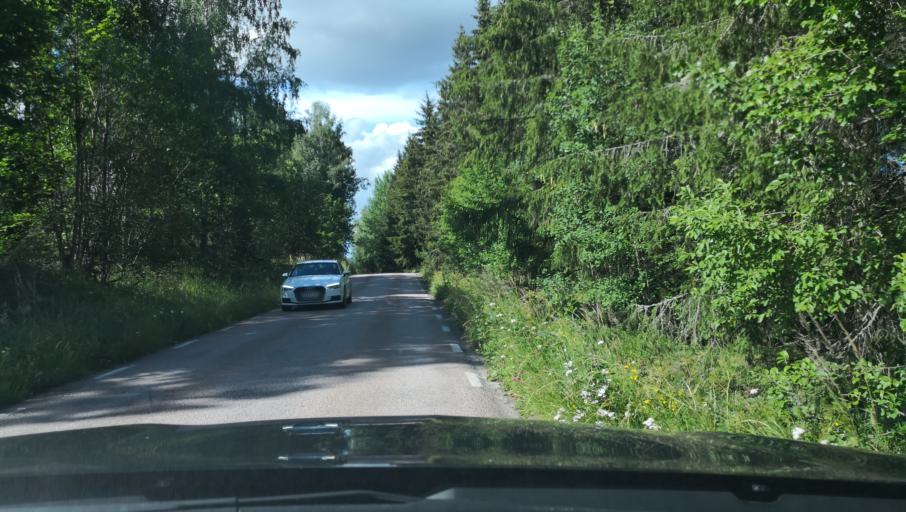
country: SE
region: Vaestmanland
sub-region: Hallstahammars Kommun
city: Hallstahammar
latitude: 59.6472
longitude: 16.2021
